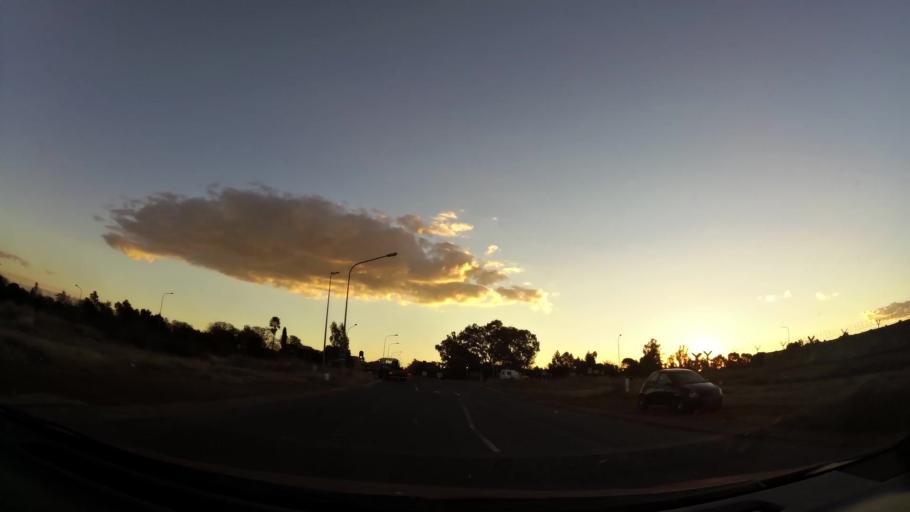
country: ZA
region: North-West
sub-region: Dr Kenneth Kaunda District Municipality
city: Potchefstroom
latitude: -26.6894
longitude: 27.0782
